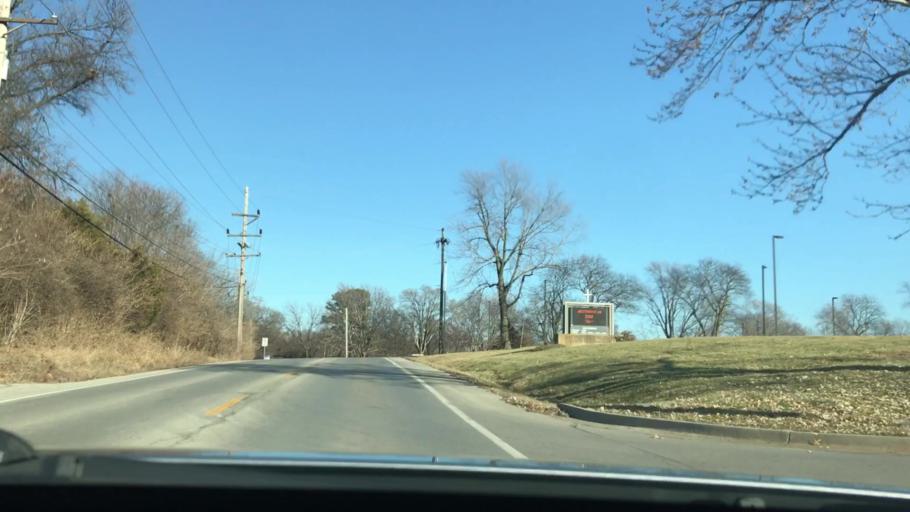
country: US
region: Missouri
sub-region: Platte County
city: Parkville
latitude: 39.2202
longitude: -94.6644
